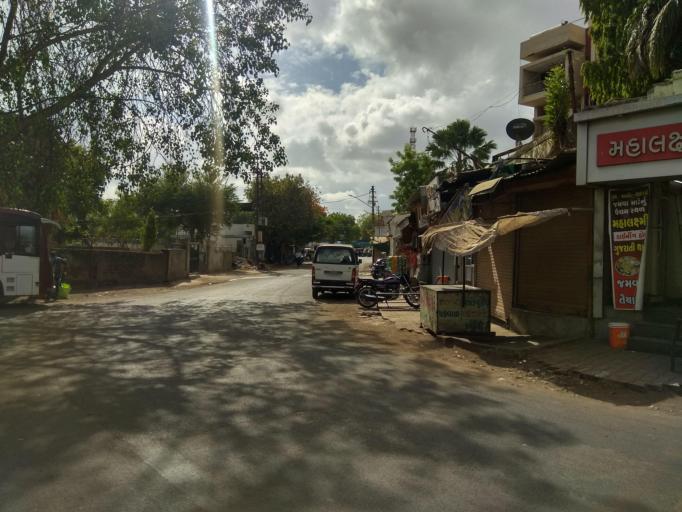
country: IN
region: Gujarat
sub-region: Bhavnagar
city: Bhavnagar
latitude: 21.7705
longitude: 72.1357
